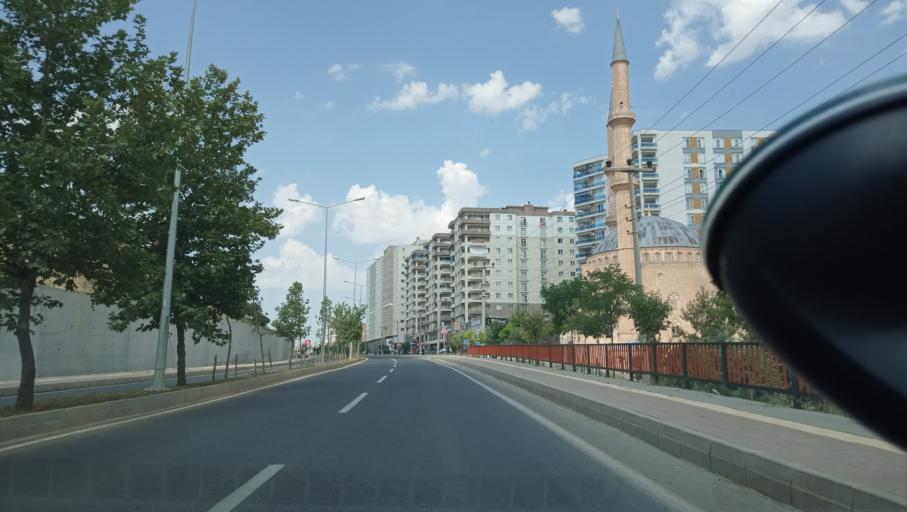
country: TR
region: Mardin
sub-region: Mardin Ilcesi
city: Mardin
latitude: 37.3220
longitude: 40.7332
